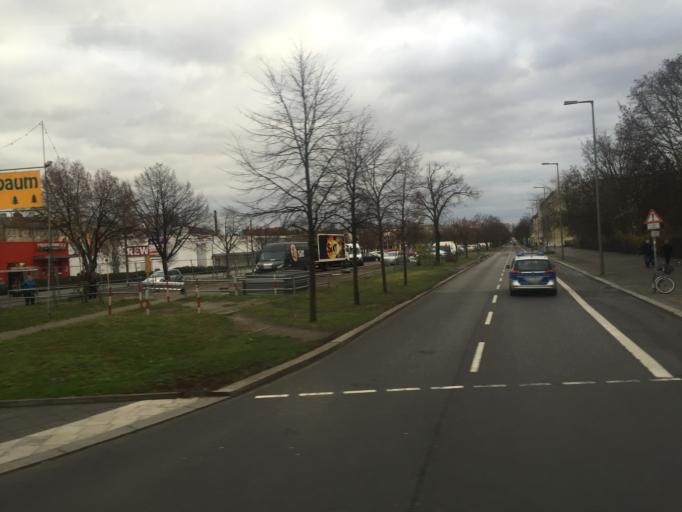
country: DE
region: Berlin
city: Prenzlauer Berg Bezirk
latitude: 52.5509
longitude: 13.4303
